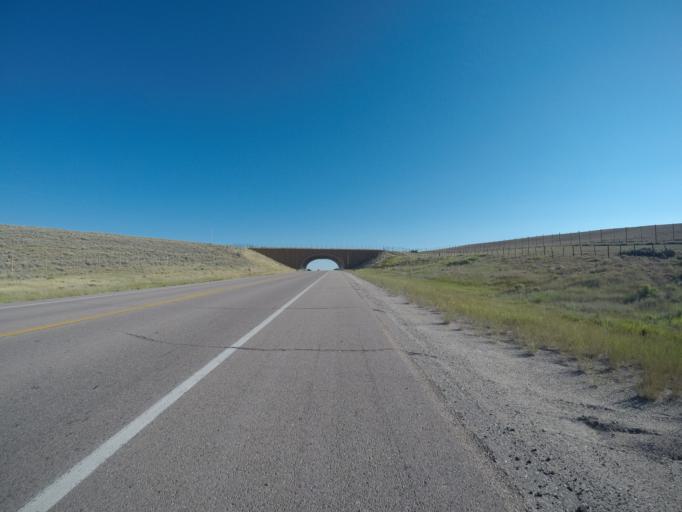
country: US
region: Wyoming
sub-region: Sublette County
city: Pinedale
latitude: 42.9115
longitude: -110.0780
